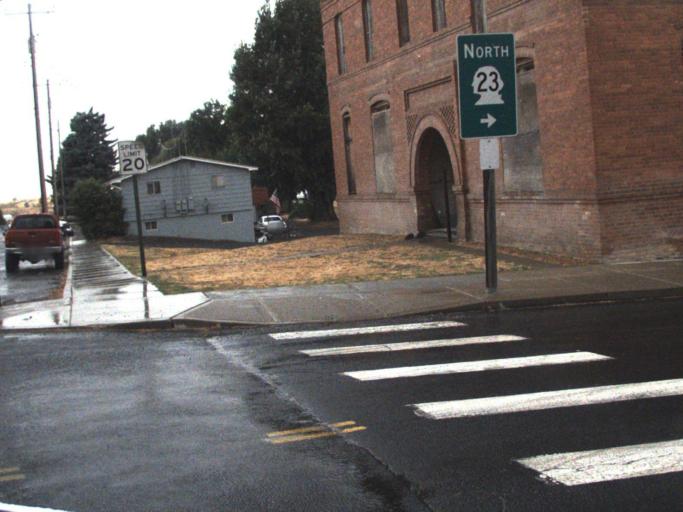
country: US
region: Washington
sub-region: Lincoln County
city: Davenport
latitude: 47.4789
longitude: -118.2547
